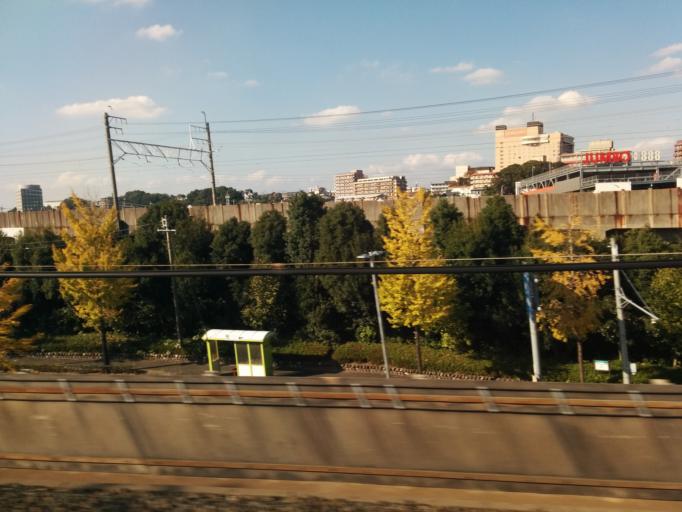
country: JP
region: Shizuoka
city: Hamamatsu
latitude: 34.6972
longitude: 137.7255
